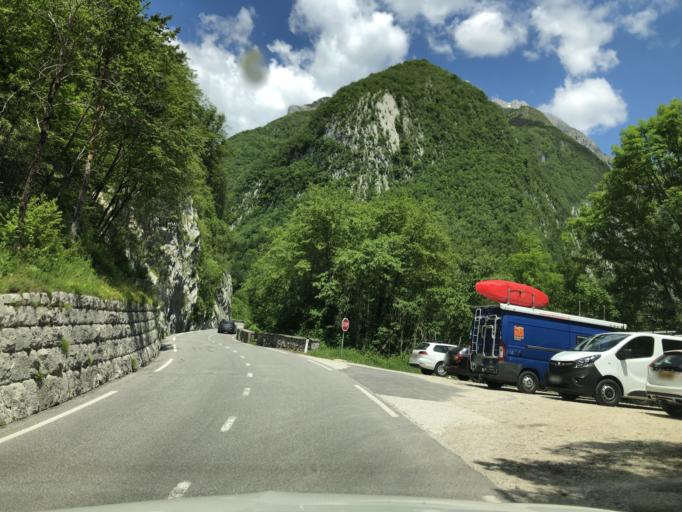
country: SI
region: Bovec
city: Bovec
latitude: 46.3591
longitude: 13.5896
